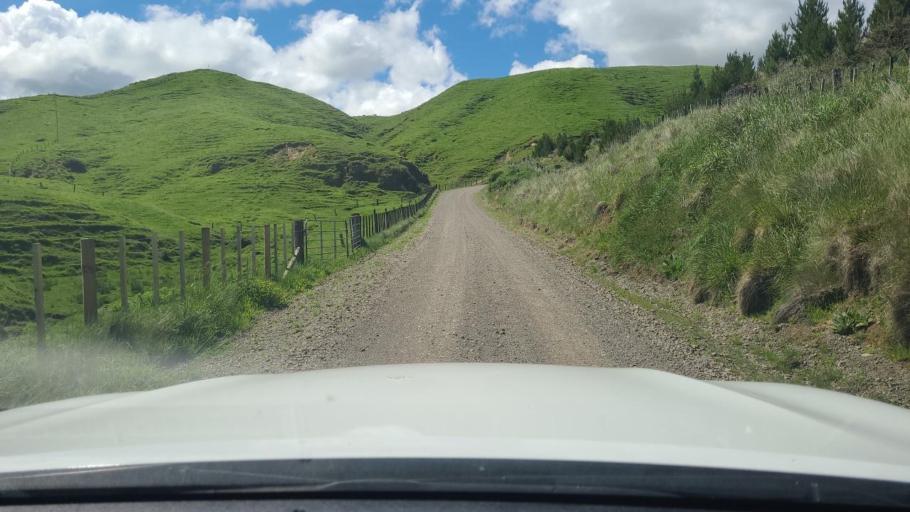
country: NZ
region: Hawke's Bay
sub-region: Napier City
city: Napier
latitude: -39.1602
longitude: 176.6631
